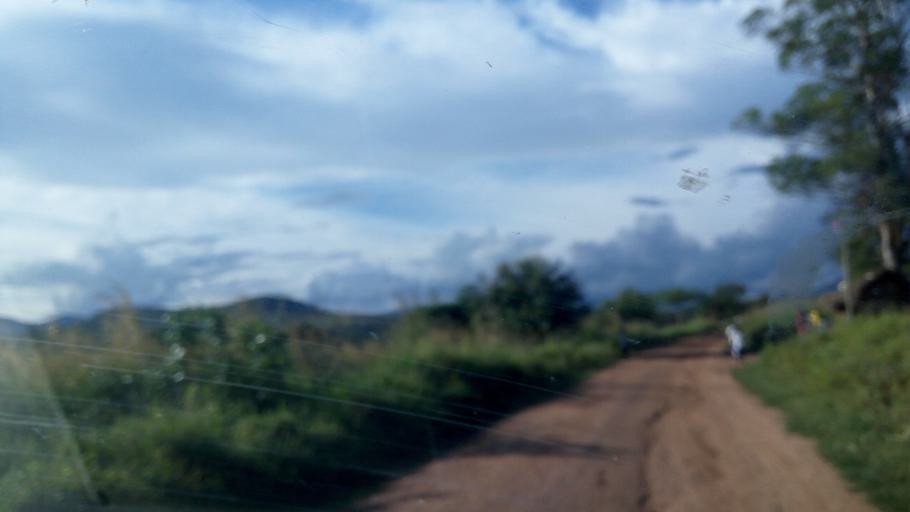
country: TZ
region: Kigoma
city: Kigoma
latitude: -4.6542
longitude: 28.7676
